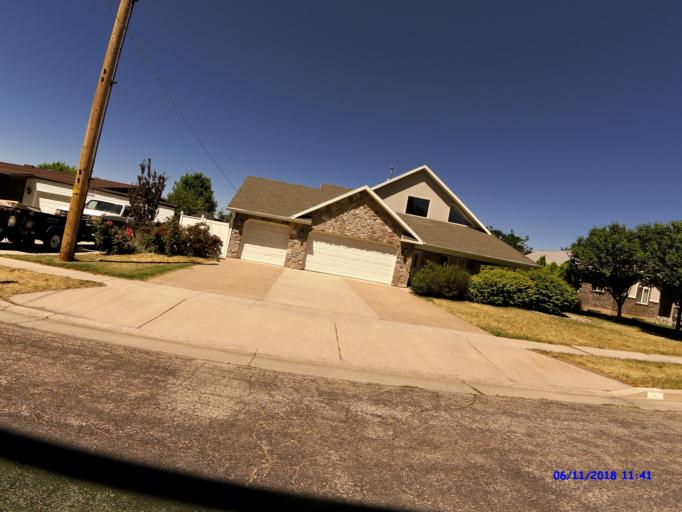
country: US
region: Utah
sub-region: Weber County
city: Ogden
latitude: 41.2302
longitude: -111.9436
